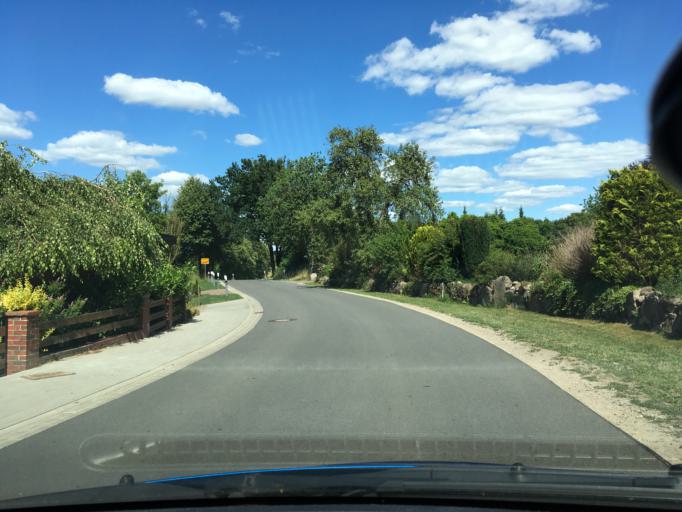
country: DE
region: Lower Saxony
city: Neu Darchau
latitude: 53.2027
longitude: 10.8599
